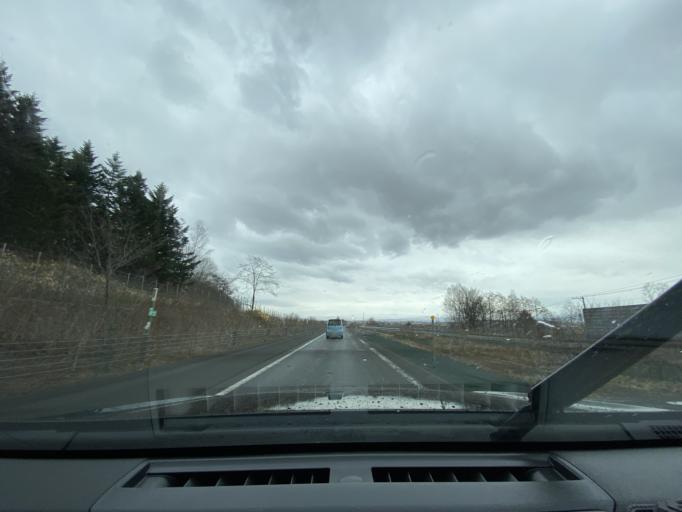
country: JP
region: Hokkaido
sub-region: Asahikawa-shi
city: Asahikawa
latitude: 43.8677
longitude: 142.4458
